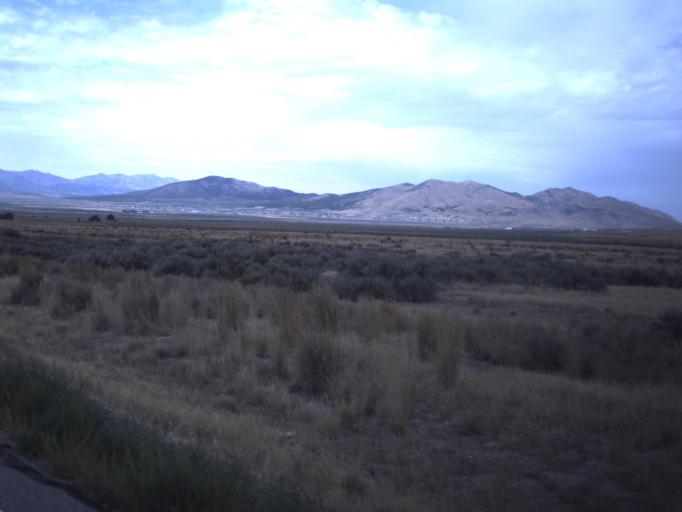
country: US
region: Utah
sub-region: Tooele County
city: Tooele
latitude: 40.3755
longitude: -112.3710
